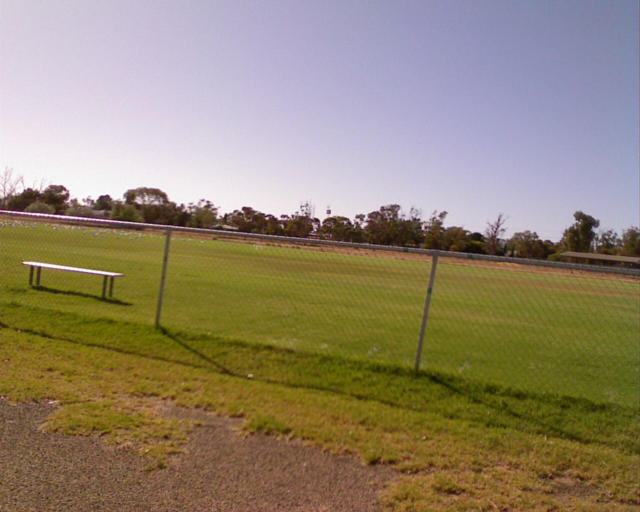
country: AU
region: Western Australia
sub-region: Wongan-Ballidu
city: Wongan Hills
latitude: -30.2747
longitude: 116.6572
